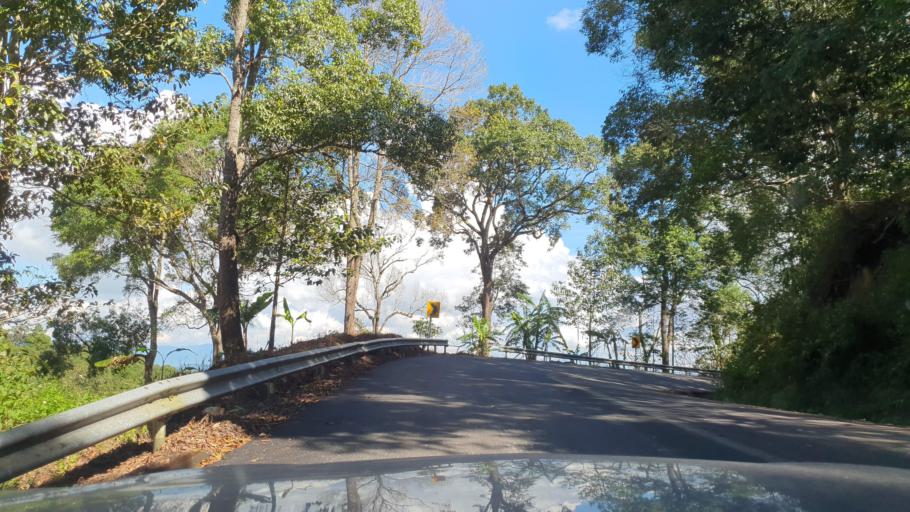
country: TH
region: Chiang Mai
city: Phrao
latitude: 19.3175
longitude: 99.3284
